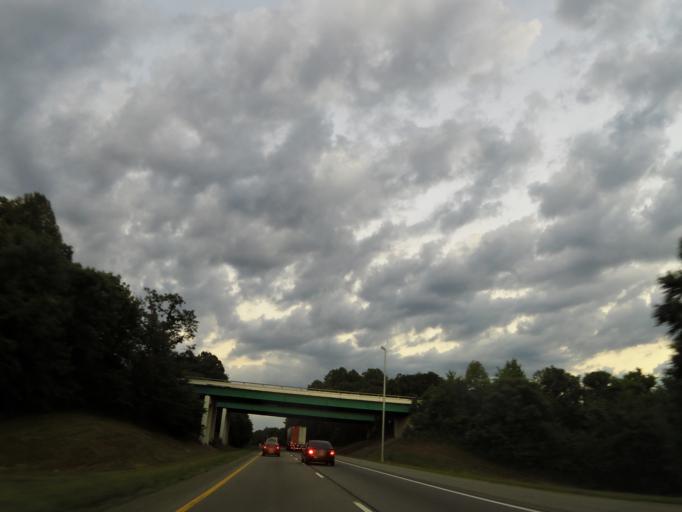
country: US
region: Tennessee
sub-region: Putnam County
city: Cookeville
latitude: 36.1345
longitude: -85.4809
